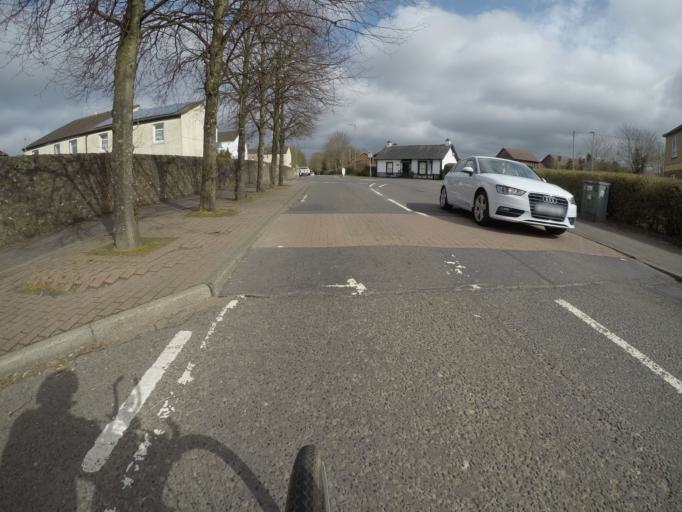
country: GB
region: Scotland
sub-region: North Ayrshire
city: Irvine
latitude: 55.6290
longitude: -4.6377
